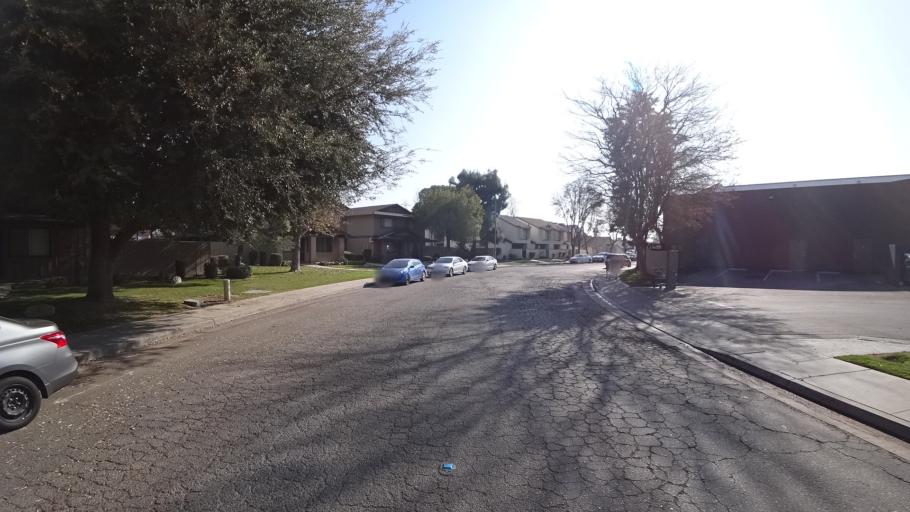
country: US
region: California
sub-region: Kern County
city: Greenacres
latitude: 35.3193
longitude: -119.0715
